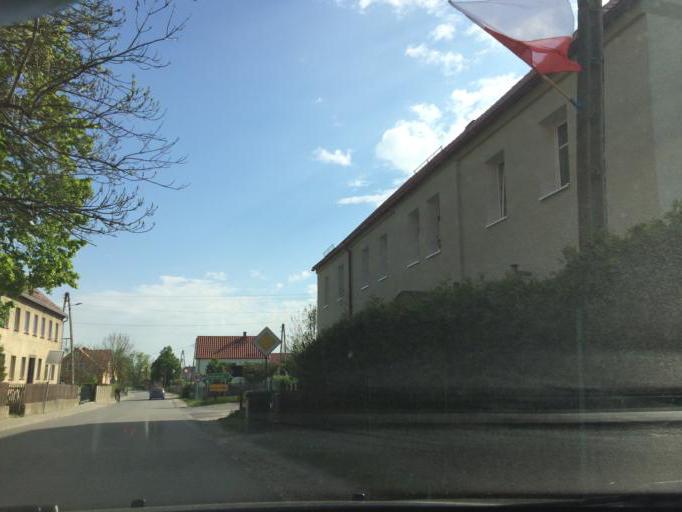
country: PL
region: Lower Silesian Voivodeship
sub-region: Powiat dzierzoniowski
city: Pieszyce
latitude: 50.7536
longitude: 16.5294
